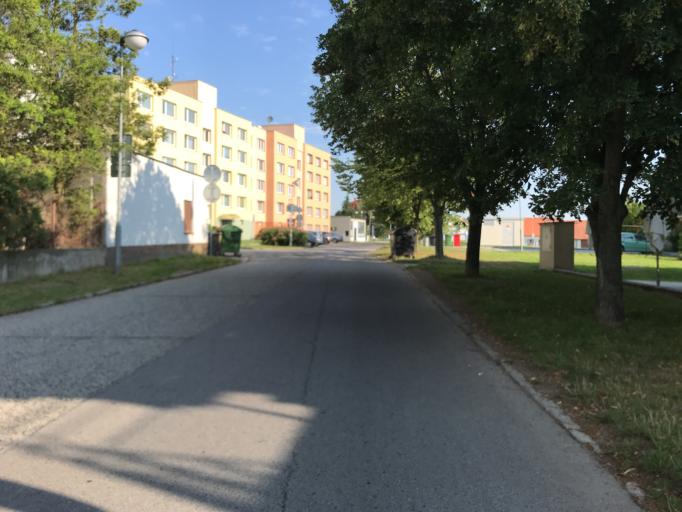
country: CZ
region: Jihocesky
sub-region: Okres Jindrichuv Hradec
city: Trebon
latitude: 49.0029
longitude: 14.7548
